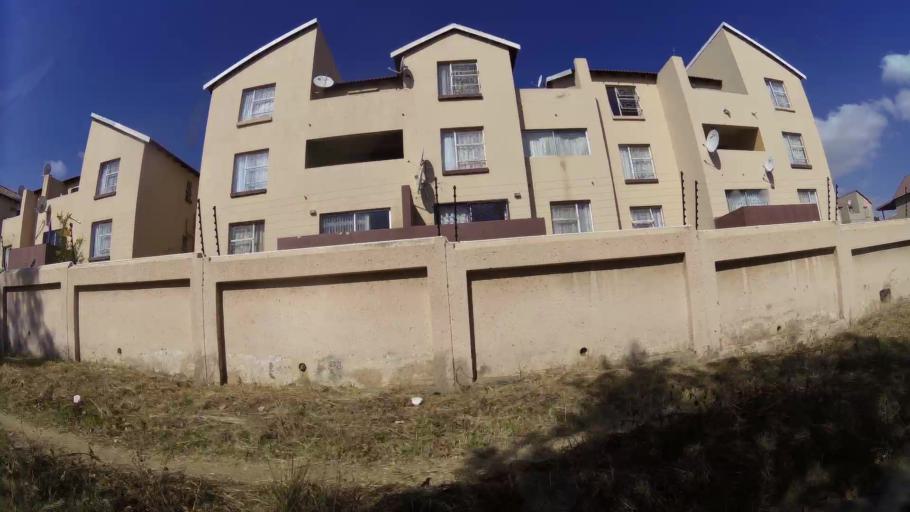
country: ZA
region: Gauteng
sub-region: City of Johannesburg Metropolitan Municipality
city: Midrand
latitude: -26.0029
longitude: 28.1118
